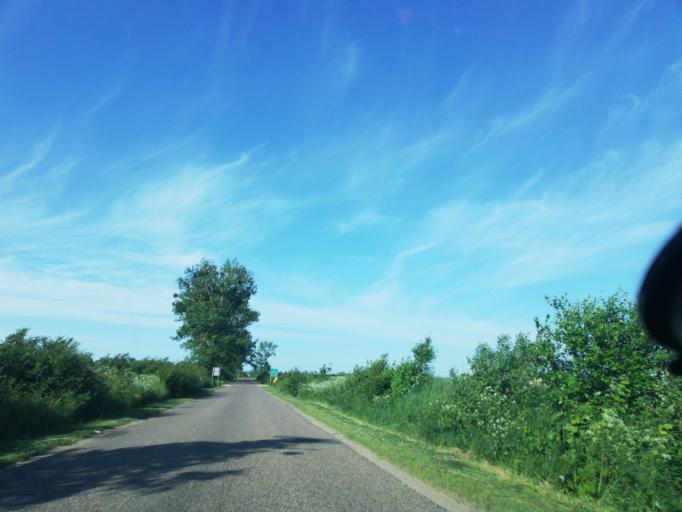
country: PL
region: Kujawsko-Pomorskie
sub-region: Powiat golubsko-dobrzynski
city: Golub-Dobrzyn
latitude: 53.0311
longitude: 19.0721
